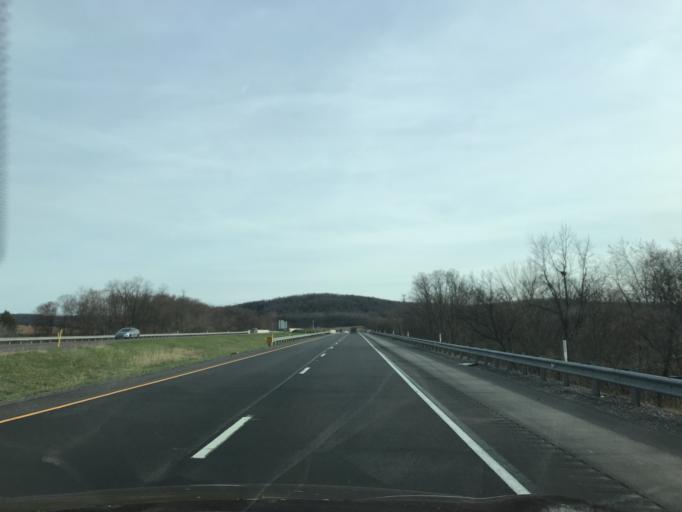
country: US
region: Pennsylvania
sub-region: Lycoming County
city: Muncy
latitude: 41.2036
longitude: -76.7689
